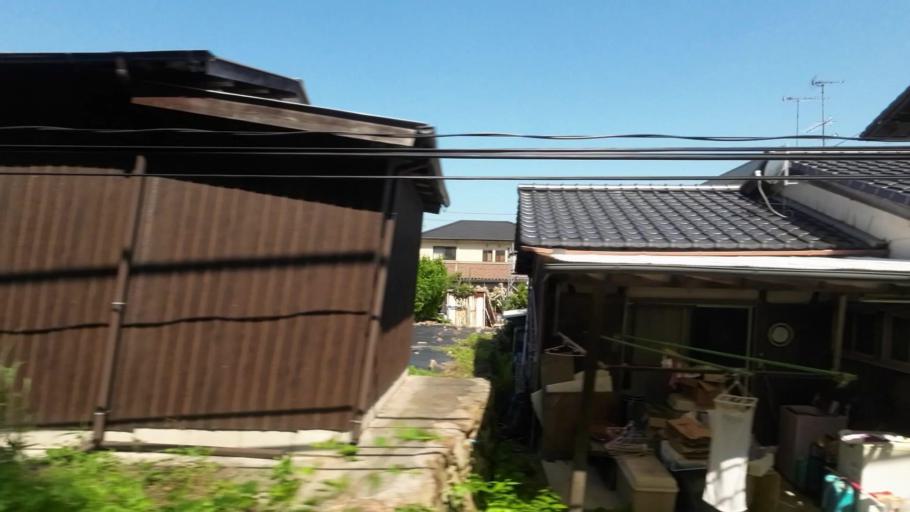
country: JP
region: Ehime
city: Kawanoecho
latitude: 34.0359
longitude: 133.5948
